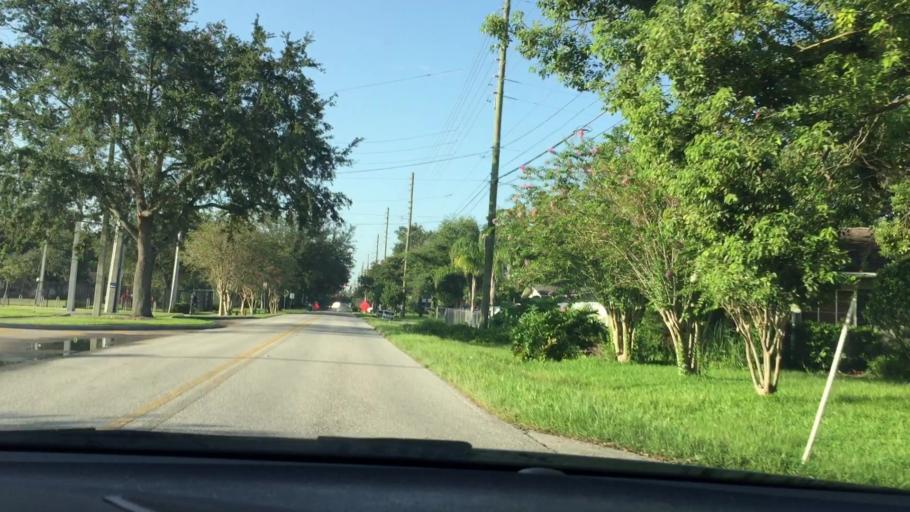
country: US
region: Florida
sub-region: Orange County
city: Fairview Shores
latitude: 28.5739
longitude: -81.4019
